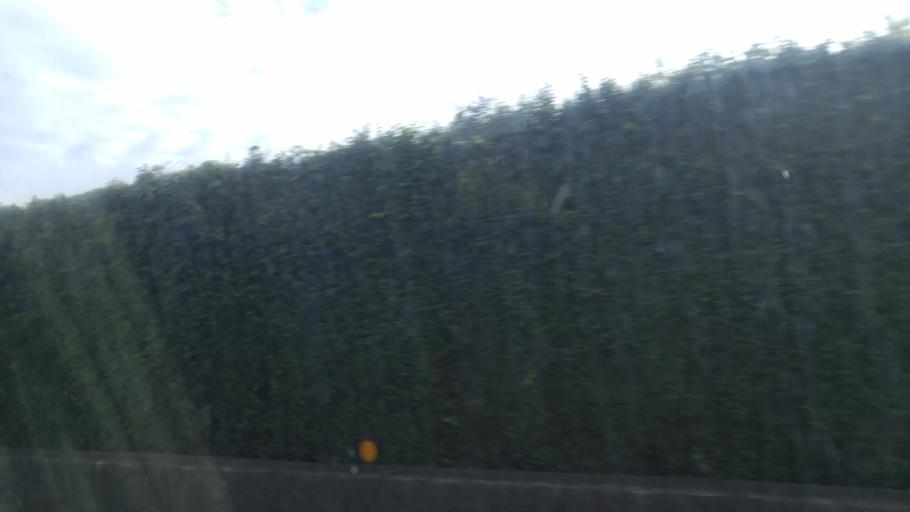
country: TW
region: Taiwan
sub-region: Hsinchu
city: Zhubei
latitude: 24.8931
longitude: 121.1232
